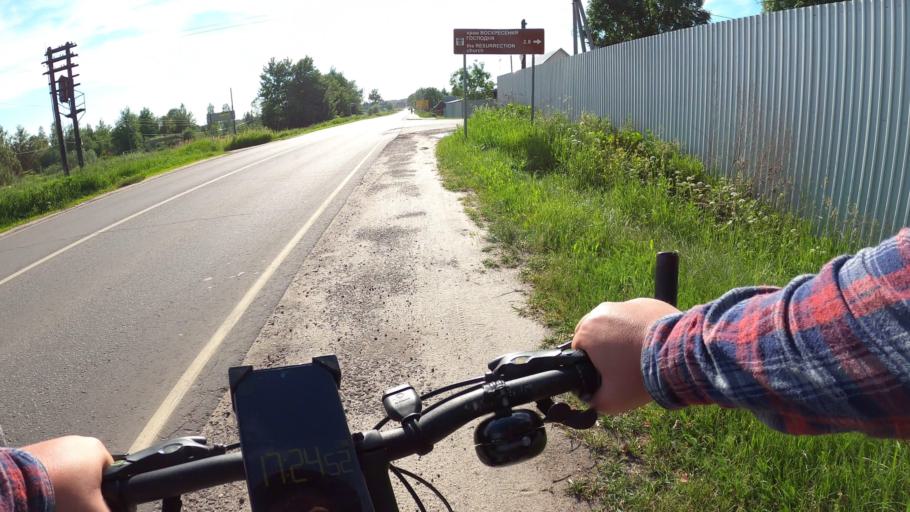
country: RU
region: Moskovskaya
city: Ashitkovo
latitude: 55.4334
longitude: 38.6044
